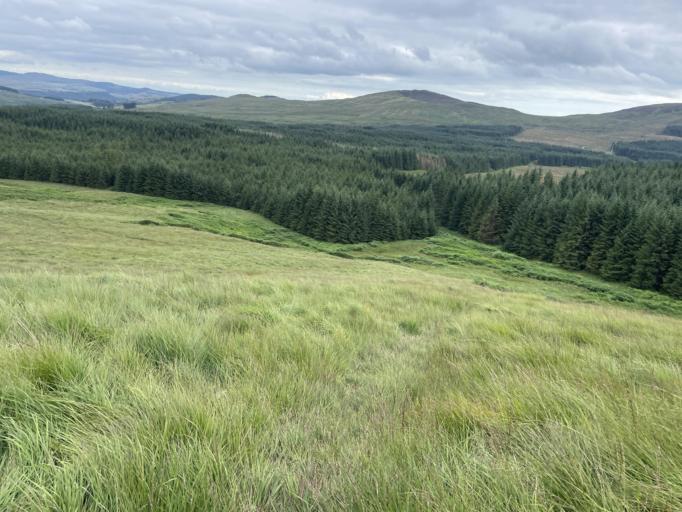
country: GB
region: Scotland
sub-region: Dumfries and Galloway
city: Newton Stewart
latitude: 54.9478
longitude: -4.2849
